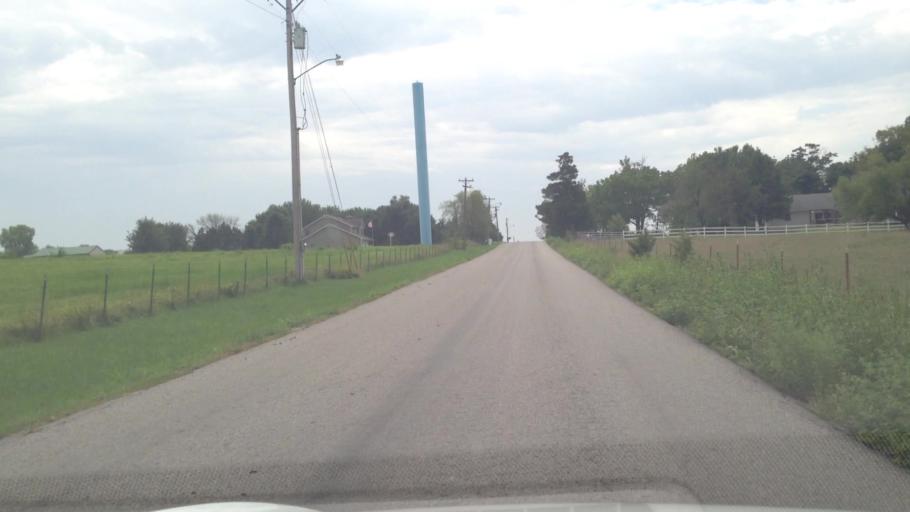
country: US
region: Kansas
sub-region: Crawford County
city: Girard
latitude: 37.5114
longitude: -94.8699
